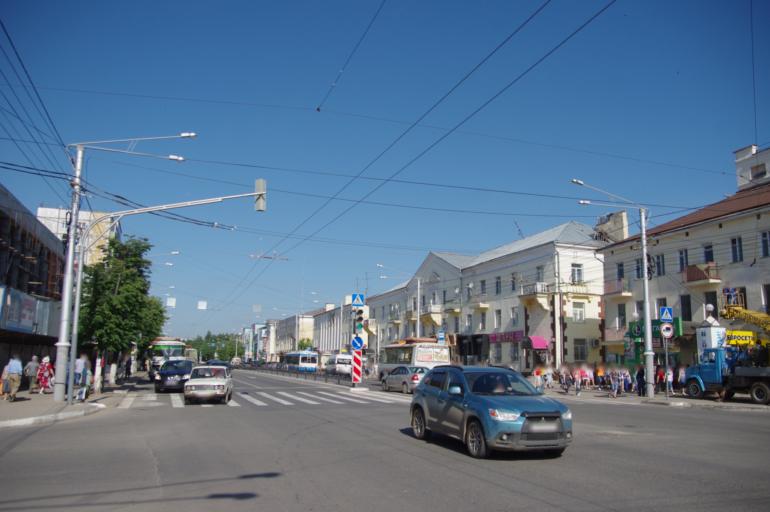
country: RU
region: Kaluga
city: Kaluga
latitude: 54.5150
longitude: 36.2507
